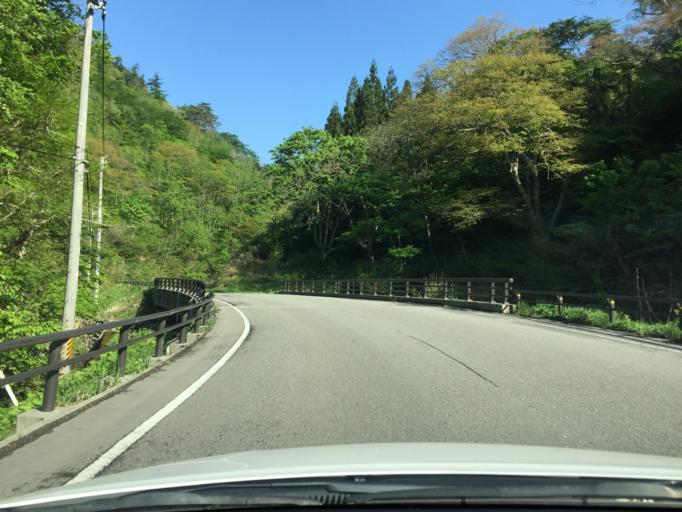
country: JP
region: Fukushima
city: Kitakata
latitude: 37.6762
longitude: 139.7256
